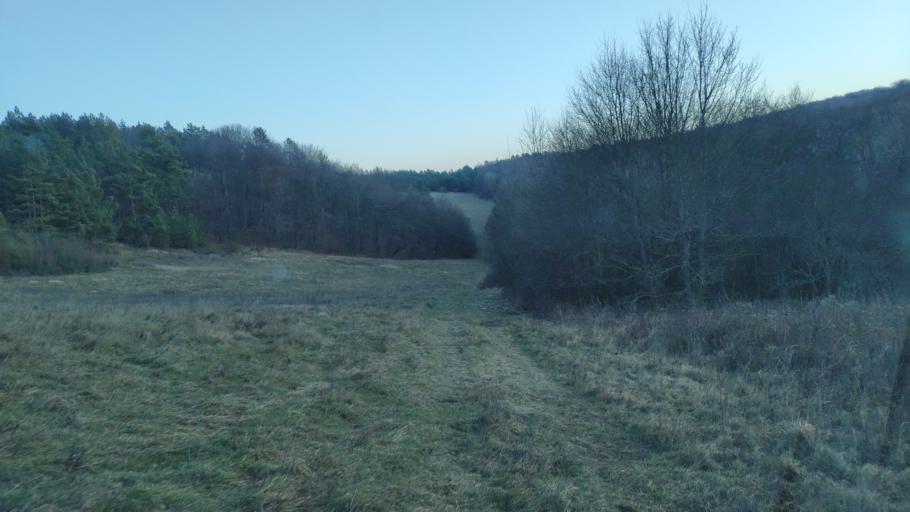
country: SK
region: Kosicky
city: Kosice
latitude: 48.8496
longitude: 21.2404
